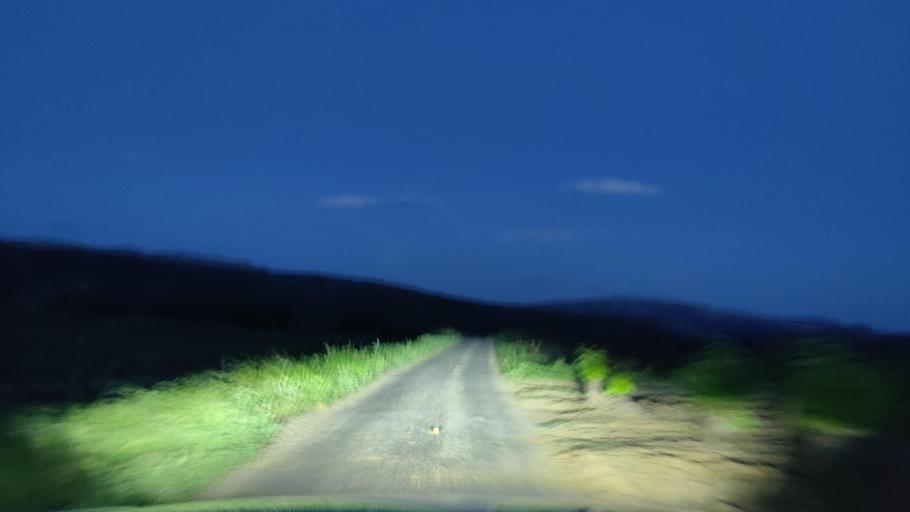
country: FR
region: Languedoc-Roussillon
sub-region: Departement des Pyrenees-Orientales
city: Estagel
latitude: 42.8789
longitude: 2.7269
